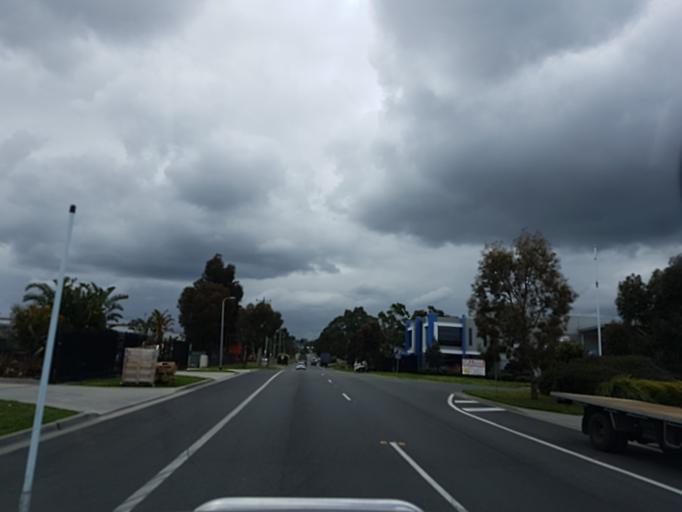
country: AU
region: Victoria
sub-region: Casey
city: Hallam
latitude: -38.0128
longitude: 145.2549
